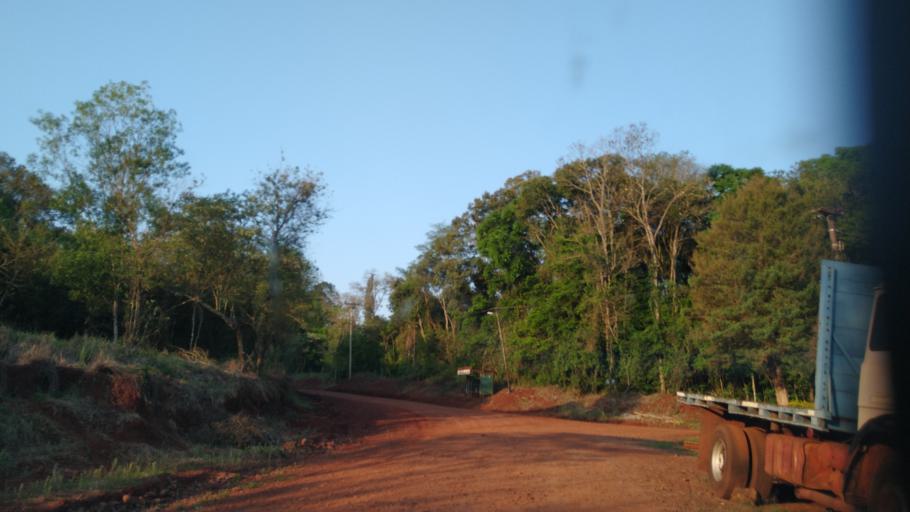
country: AR
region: Misiones
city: Jardin America
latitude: -27.0888
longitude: -55.2783
